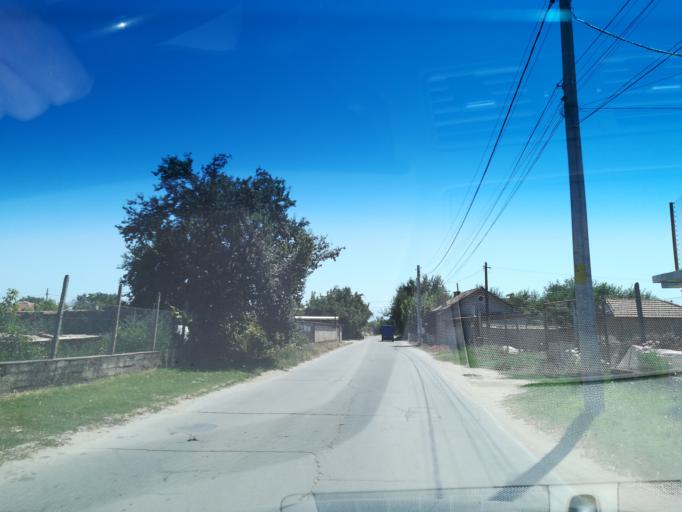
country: BG
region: Pazardzhik
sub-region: Obshtina Pazardzhik
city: Pazardzhik
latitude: 42.2780
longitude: 24.3954
